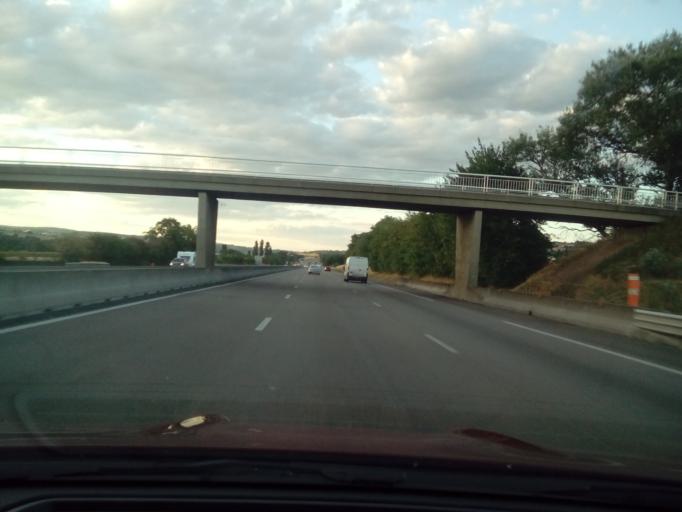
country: FR
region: Rhone-Alpes
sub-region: Departement de l'Isere
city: Auberives-sur-Vareze
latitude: 45.4455
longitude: 4.8276
